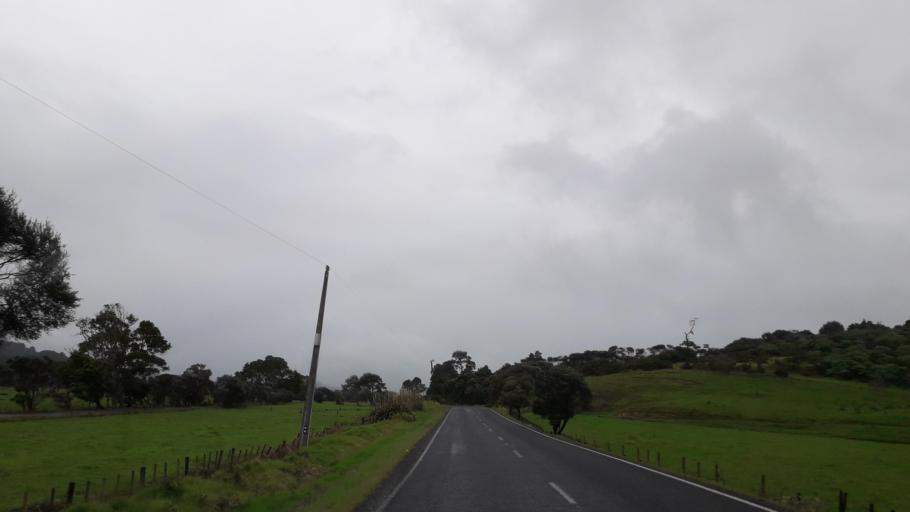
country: NZ
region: Northland
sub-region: Far North District
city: Kaitaia
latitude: -35.3633
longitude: 173.4951
